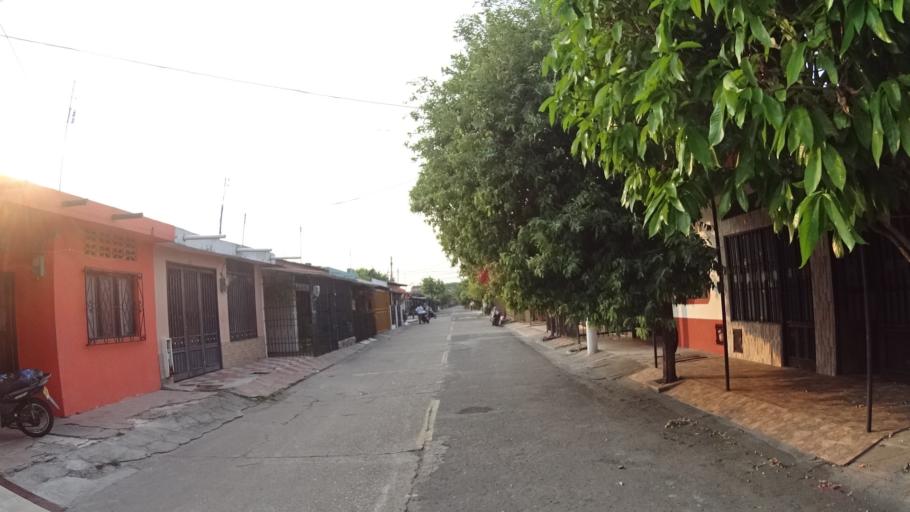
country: CO
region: Caldas
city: La Dorada
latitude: 5.4431
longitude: -74.6583
